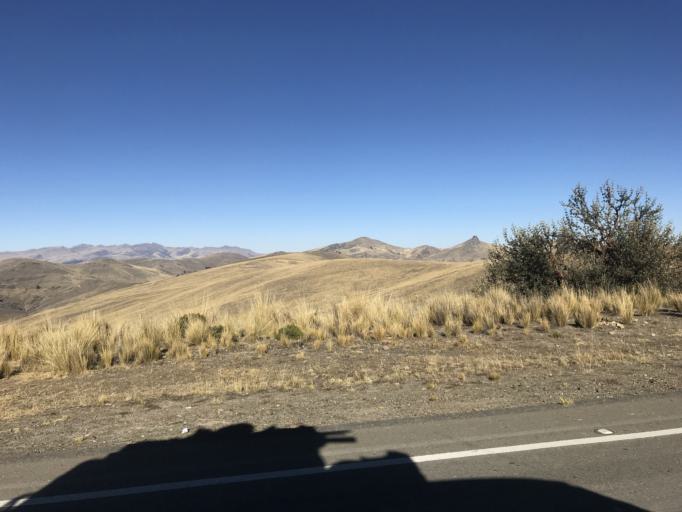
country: PE
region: Puno
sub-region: Yunguyo
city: Yunguyo
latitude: -16.1638
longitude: -68.9867
